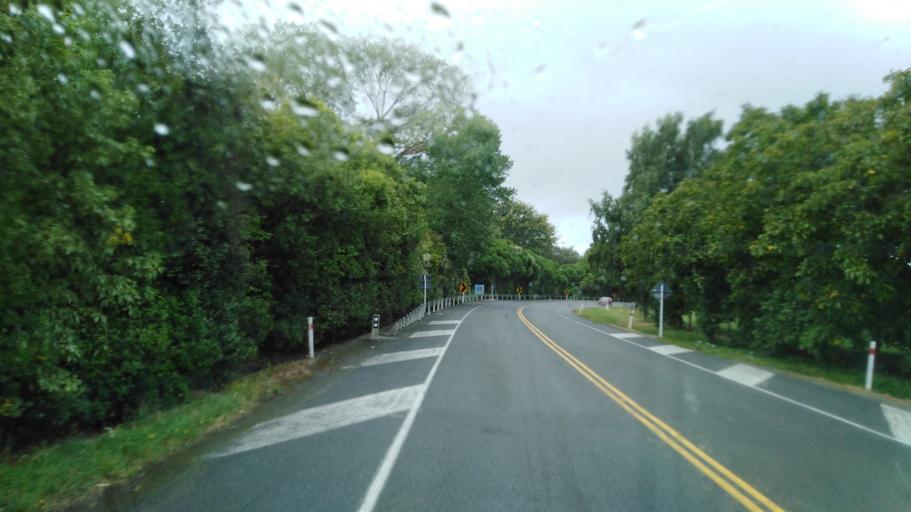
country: NZ
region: Marlborough
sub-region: Marlborough District
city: Blenheim
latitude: -41.4578
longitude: 173.9515
